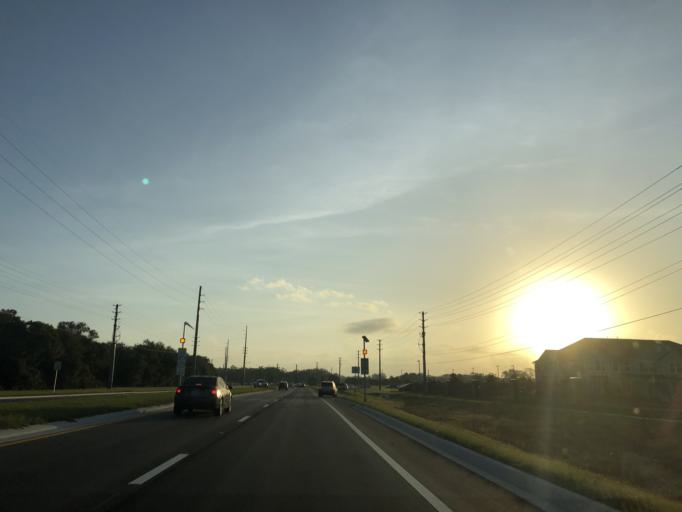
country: US
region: Florida
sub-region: Osceola County
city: Kissimmee
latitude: 28.3248
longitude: -81.4297
